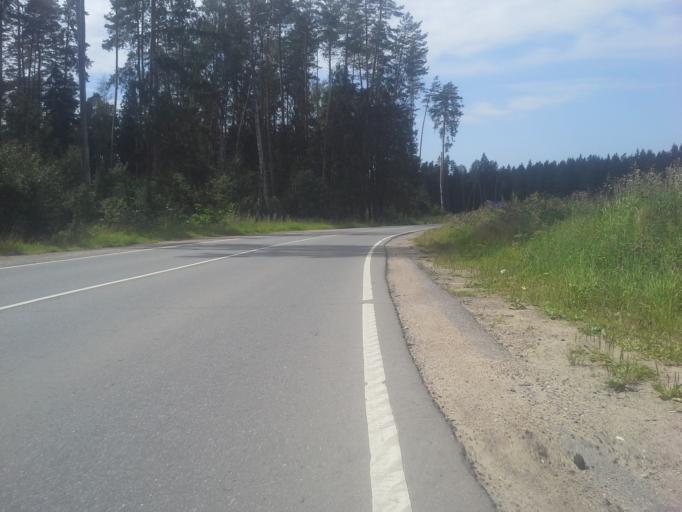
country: RU
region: Moskovskaya
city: Karinskoye
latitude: 55.6665
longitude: 36.7537
